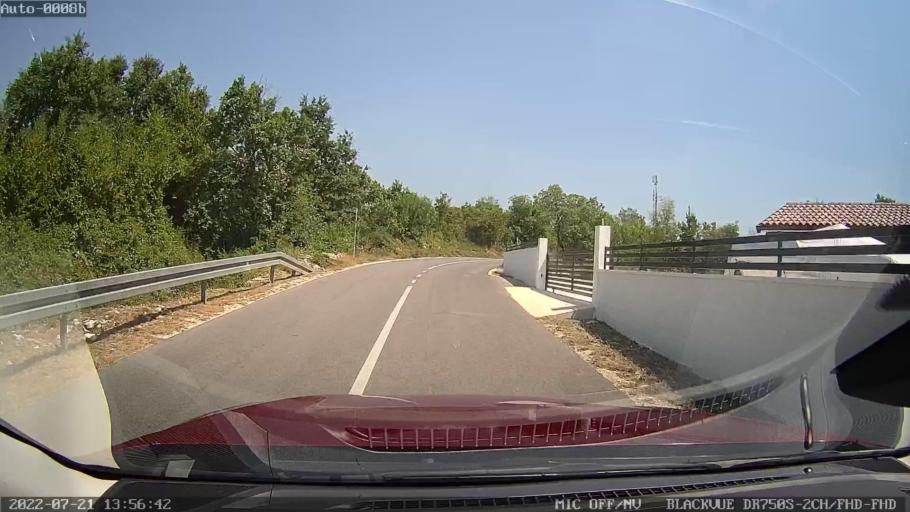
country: HR
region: Istarska
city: Pazin
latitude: 45.1189
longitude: 13.8436
